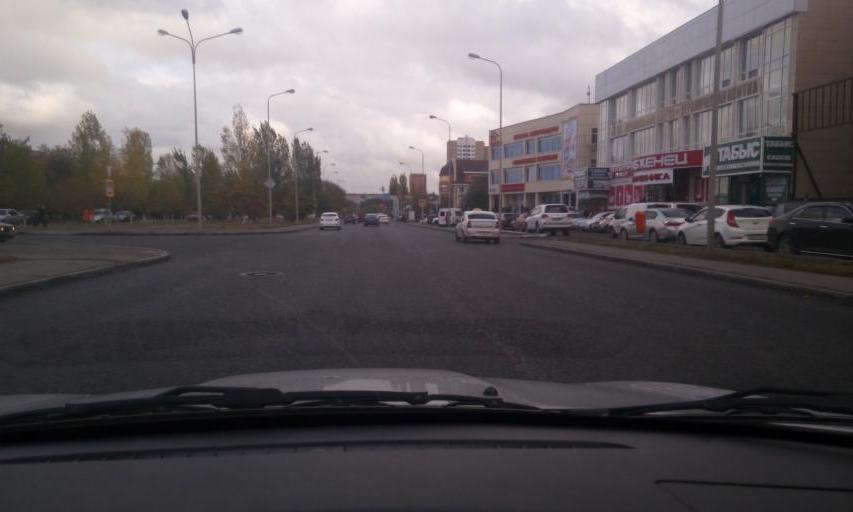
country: KZ
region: Astana Qalasy
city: Astana
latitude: 51.1647
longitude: 71.4678
